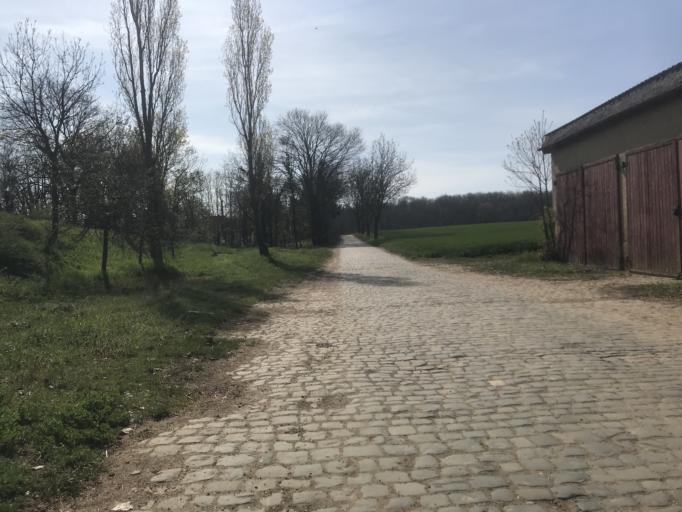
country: DE
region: Rheinland-Pfalz
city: Appenheim
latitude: 49.9389
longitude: 8.0586
